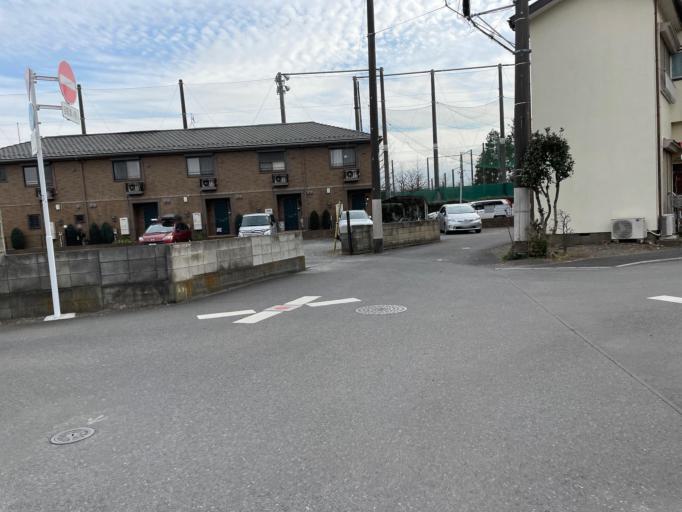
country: JP
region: Tokyo
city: Nishi-Tokyo-shi
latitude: 35.7090
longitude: 139.5378
